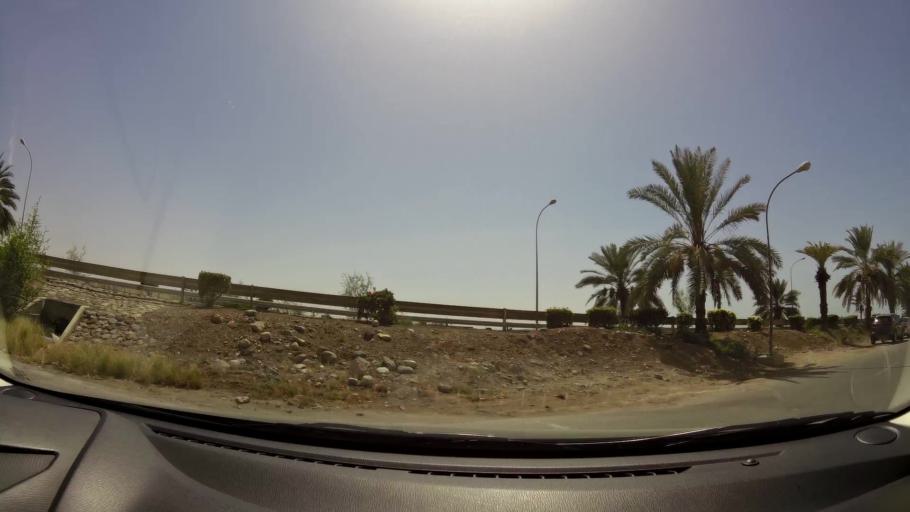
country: OM
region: Muhafazat Masqat
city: Bawshar
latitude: 23.5961
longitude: 58.3479
